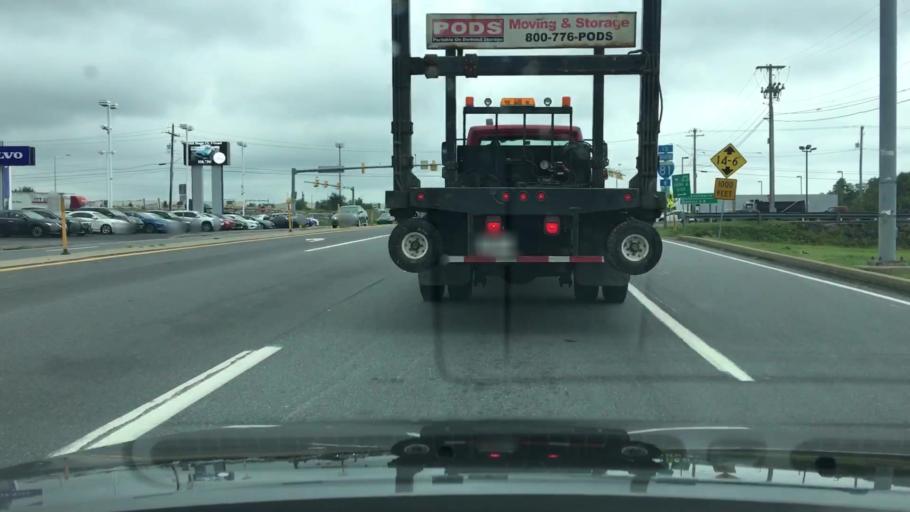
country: US
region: Pennsylvania
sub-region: Luzerne County
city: Hughestown
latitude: 41.3065
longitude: -75.7641
